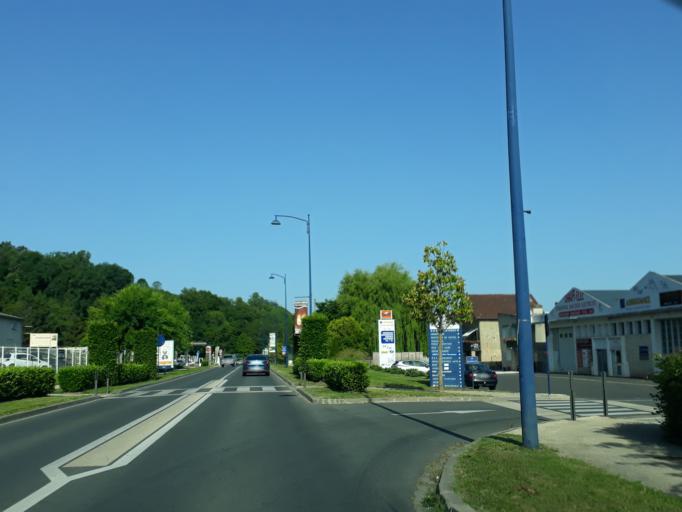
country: FR
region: Aquitaine
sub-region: Departement de la Dordogne
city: Terrasson-Lavilledieu
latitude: 45.1285
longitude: 1.3201
